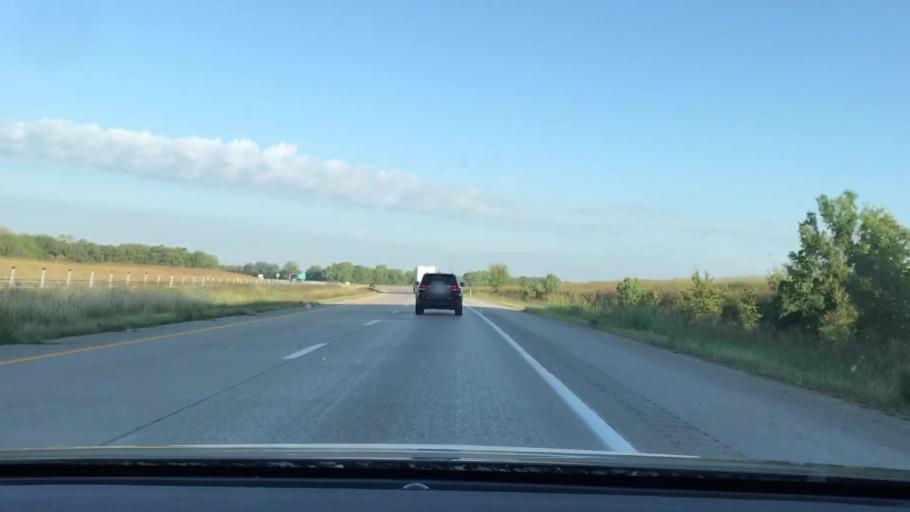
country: US
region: Kentucky
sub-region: Christian County
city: Oak Grove
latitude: 36.7290
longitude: -87.4894
